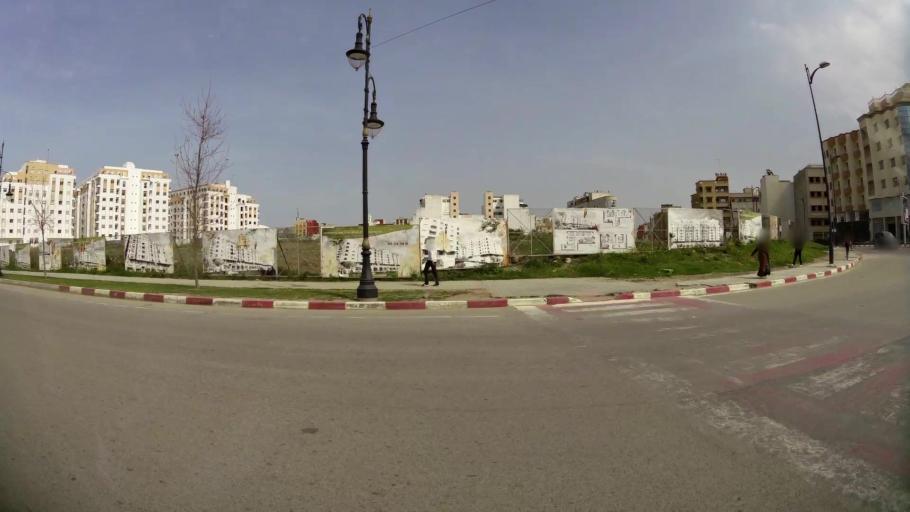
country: MA
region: Tanger-Tetouan
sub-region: Tanger-Assilah
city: Tangier
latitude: 35.7535
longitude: -5.8507
